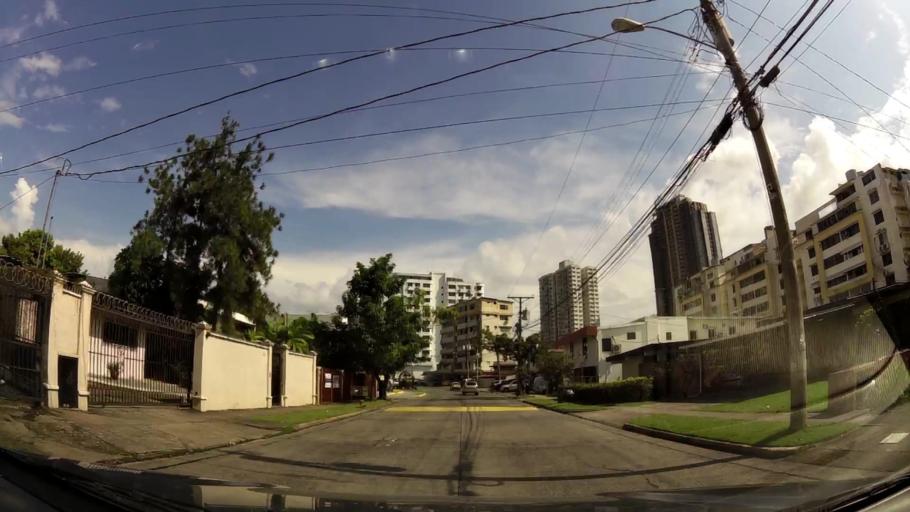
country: PA
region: Panama
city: Panama
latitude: 8.9952
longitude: -79.5211
